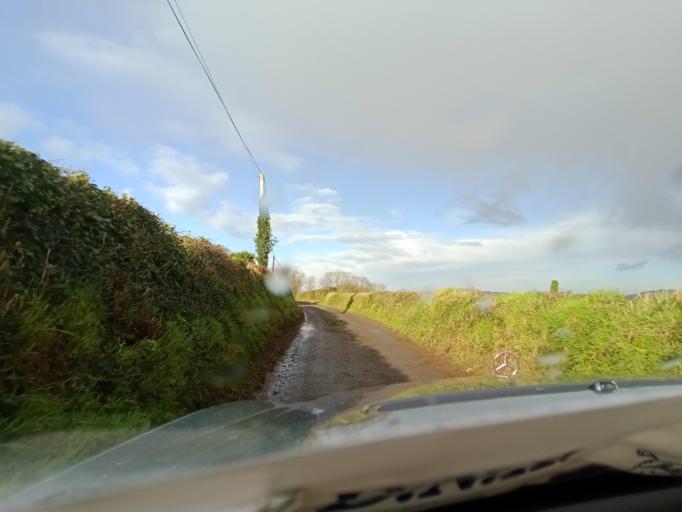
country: IE
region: Leinster
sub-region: Kilkenny
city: Mooncoin
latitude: 52.2938
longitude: -7.2678
